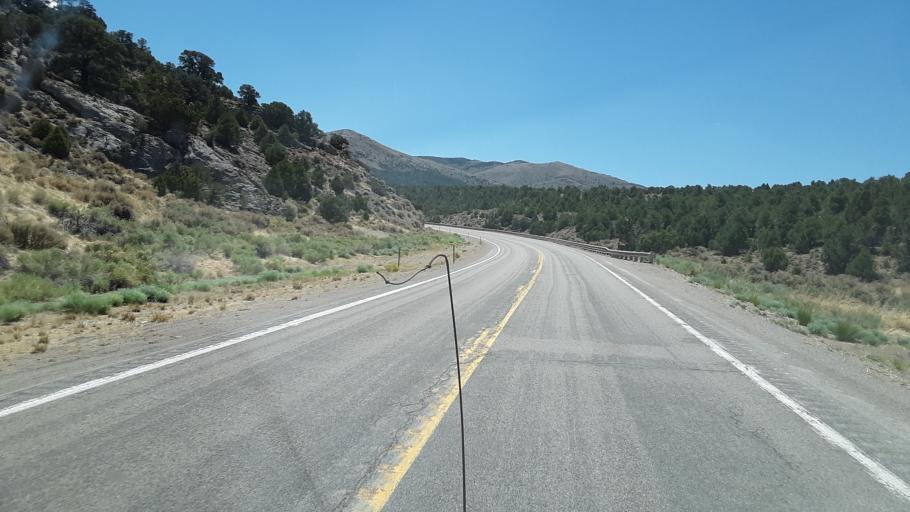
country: US
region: Nevada
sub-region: White Pine County
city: Ely
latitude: 39.0241
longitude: -114.6887
